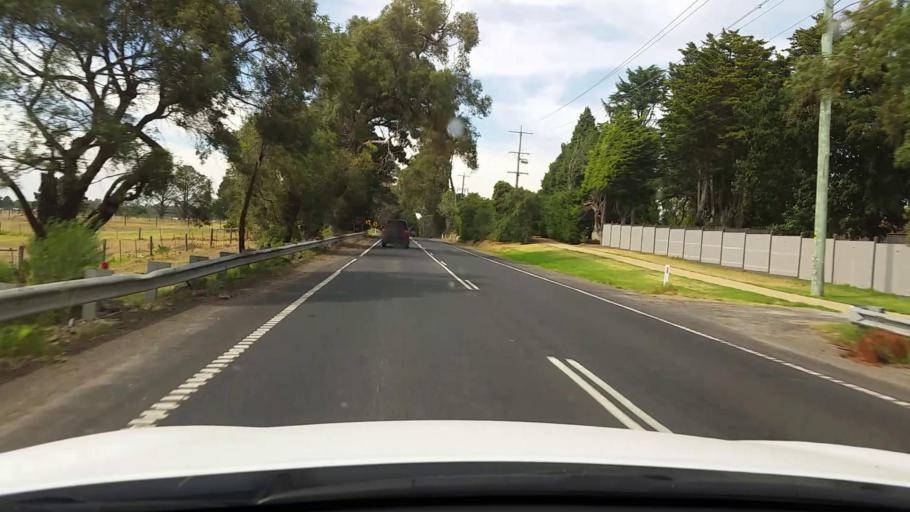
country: AU
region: Victoria
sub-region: Mornington Peninsula
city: Tyabb
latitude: -38.2437
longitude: 145.1911
